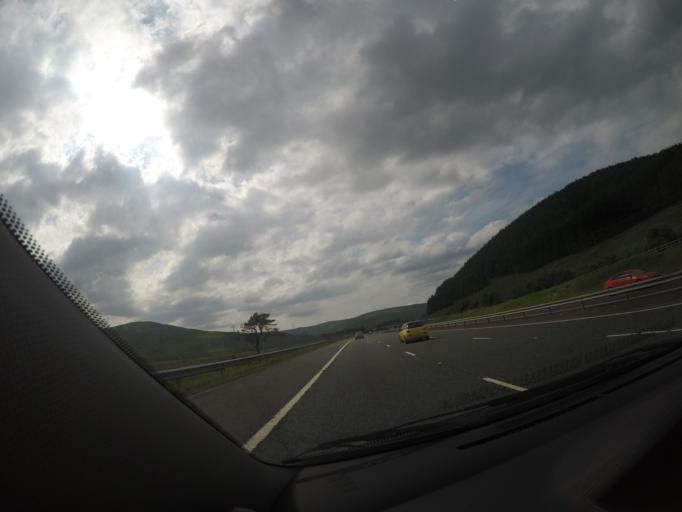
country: GB
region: Scotland
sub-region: Dumfries and Galloway
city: Moffat
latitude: 55.4304
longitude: -3.6360
